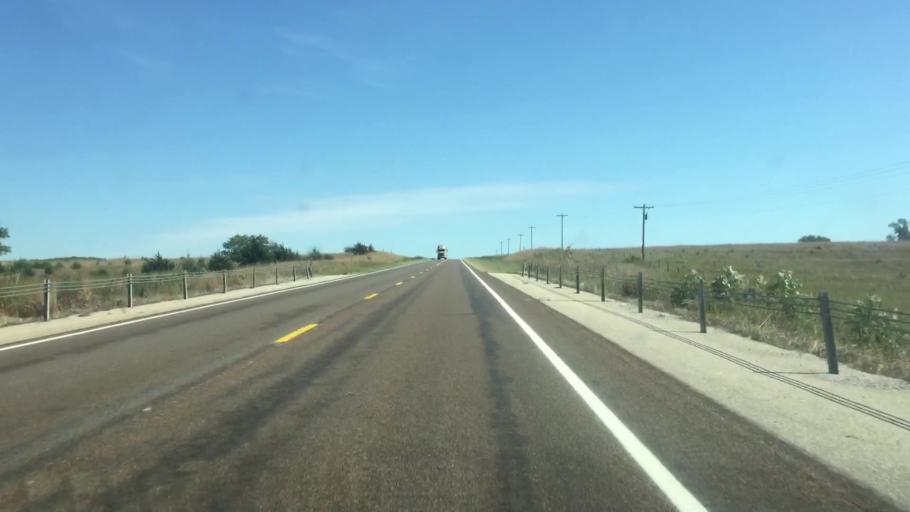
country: US
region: Nebraska
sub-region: Gage County
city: Wymore
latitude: 40.0455
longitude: -96.7734
